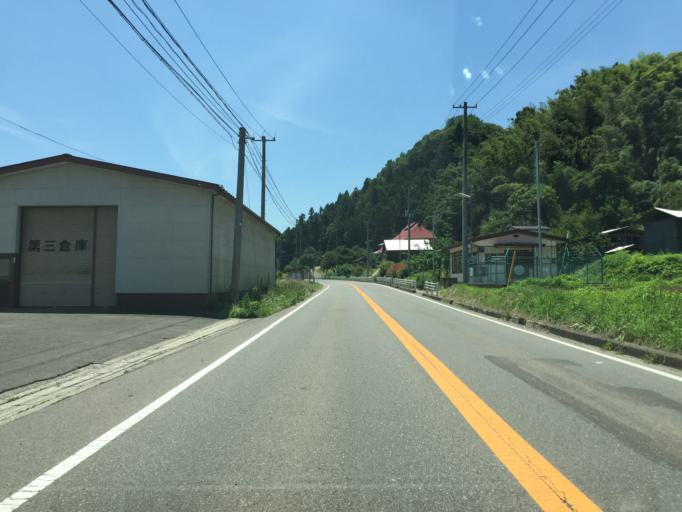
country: JP
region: Fukushima
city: Hobaramachi
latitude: 37.7631
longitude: 140.5652
